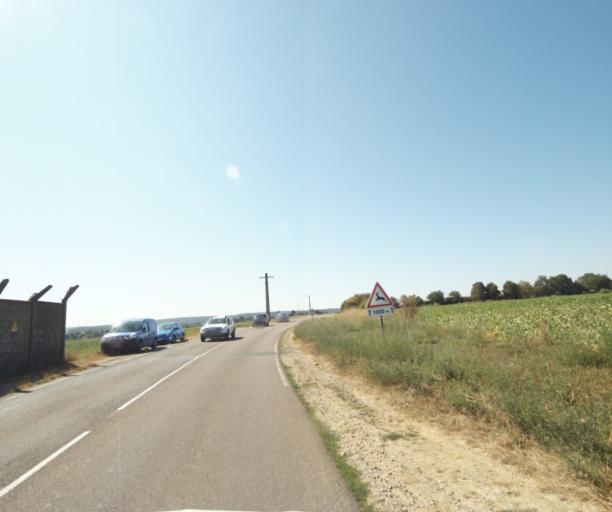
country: FR
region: Ile-de-France
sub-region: Departement de l'Essonne
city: Itteville
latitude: 48.5204
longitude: 2.3549
